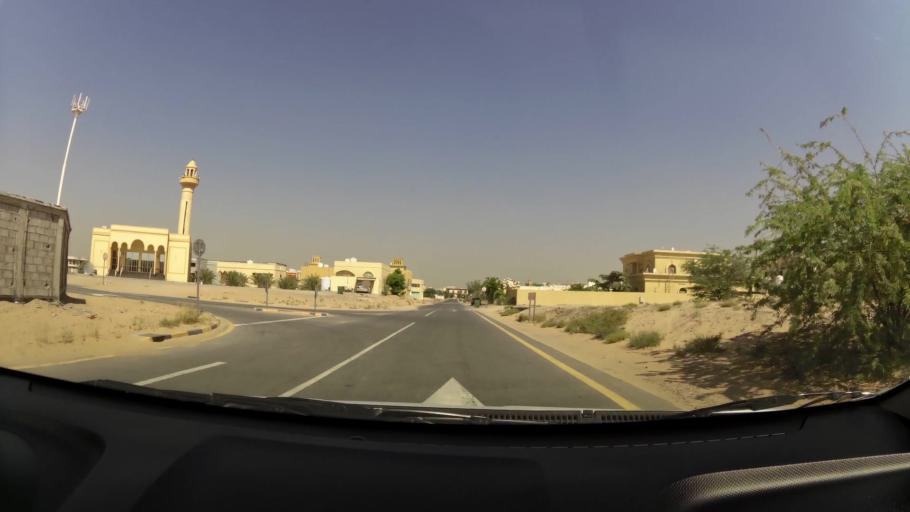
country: AE
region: Ajman
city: Ajman
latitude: 25.4102
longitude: 55.5323
